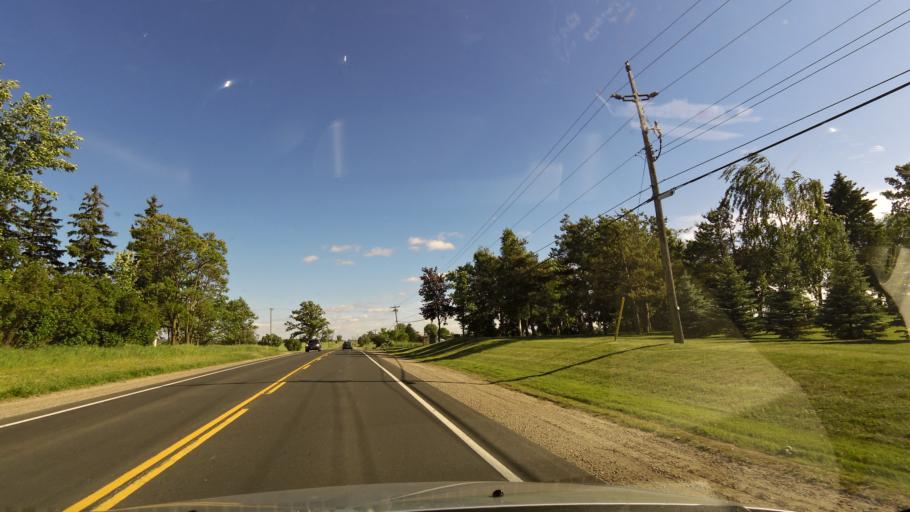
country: CA
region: Ontario
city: Bradford West Gwillimbury
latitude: 44.0615
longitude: -79.6690
